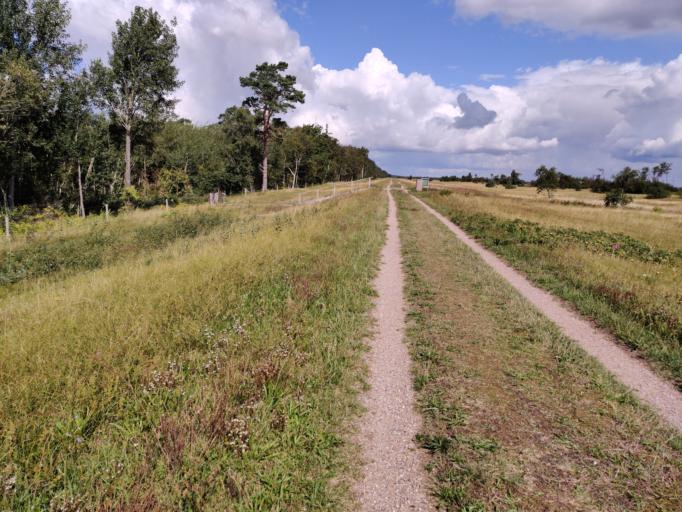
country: DK
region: Zealand
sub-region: Guldborgsund Kommune
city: Nykobing Falster
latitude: 54.6245
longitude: 11.9624
